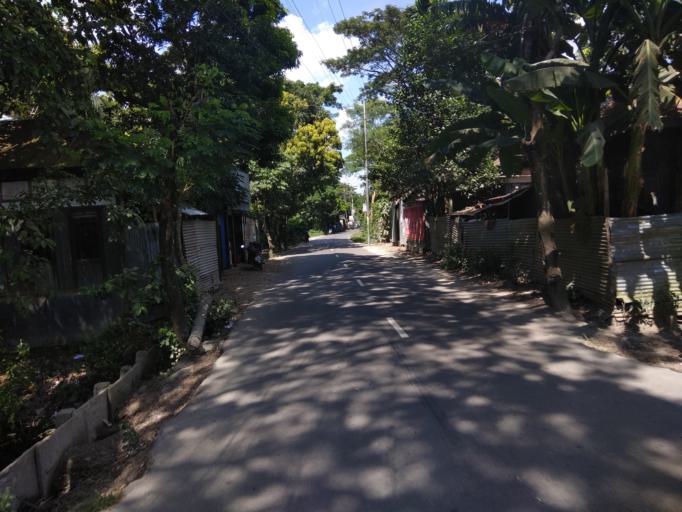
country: BD
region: Dhaka
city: Narayanganj
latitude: 23.4402
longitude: 90.4896
